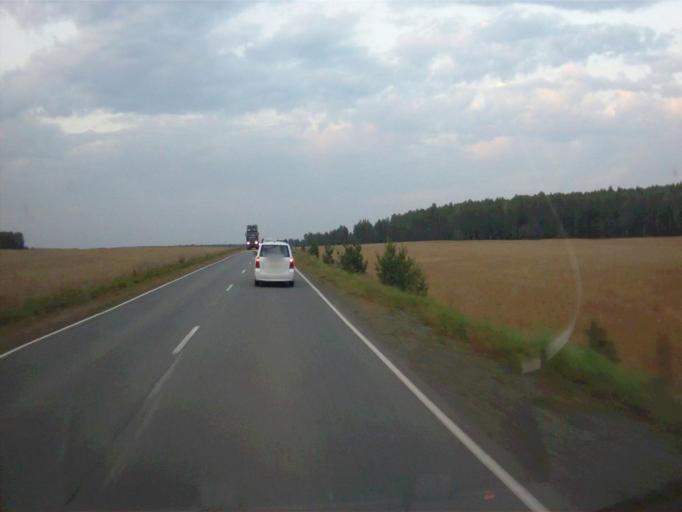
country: RU
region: Chelyabinsk
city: Chebarkul'
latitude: 55.1699
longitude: 60.4502
